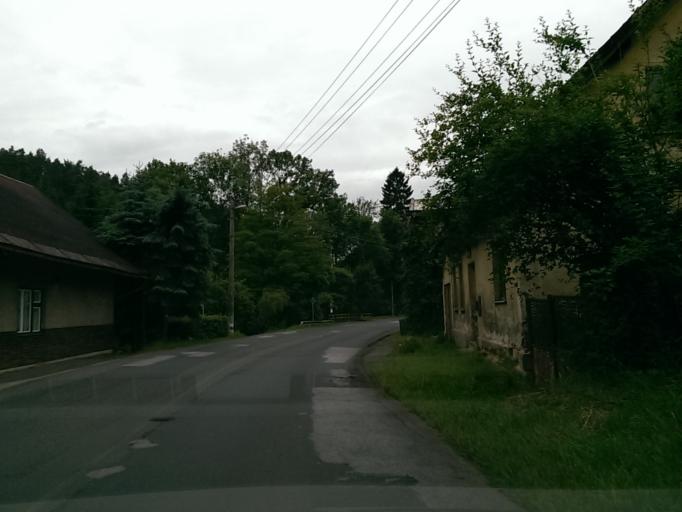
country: CZ
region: Liberecky
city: Mala Skala
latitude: 50.5869
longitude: 15.2184
